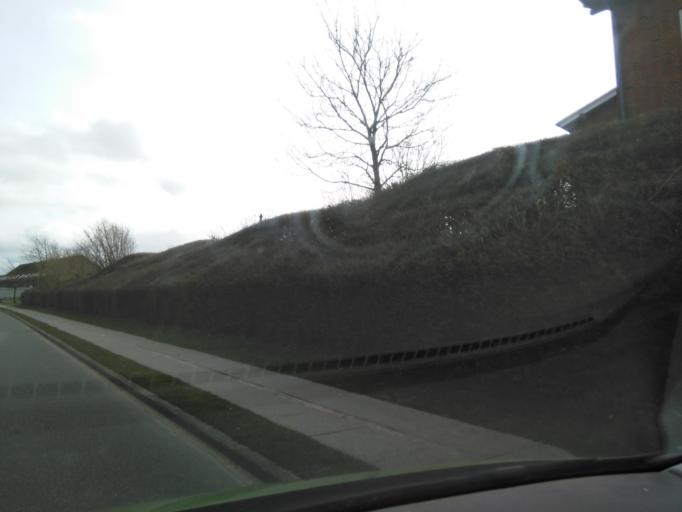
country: DK
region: Central Jutland
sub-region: Arhus Kommune
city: Arhus
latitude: 56.1926
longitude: 10.1932
